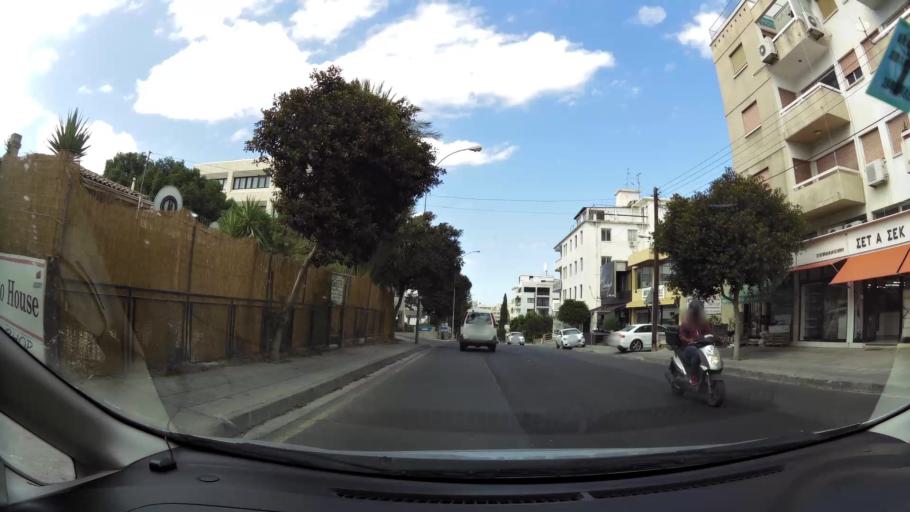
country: CY
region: Lefkosia
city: Nicosia
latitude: 35.1586
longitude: 33.3641
